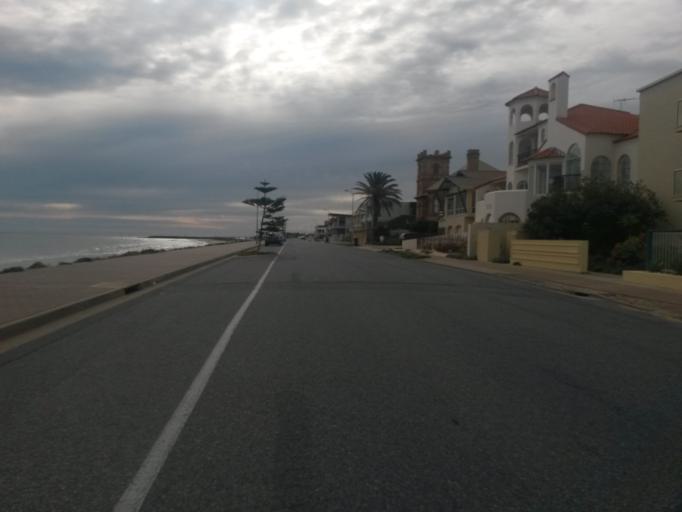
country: AU
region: South Australia
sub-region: Adelaide
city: Glenelg
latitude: -34.9685
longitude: 138.5103
